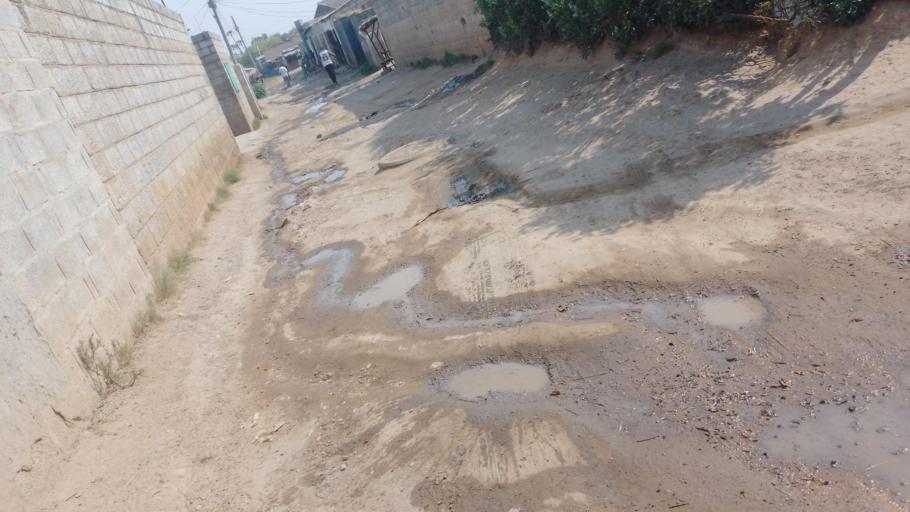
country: ZM
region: Lusaka
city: Lusaka
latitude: -15.4015
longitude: 28.3651
